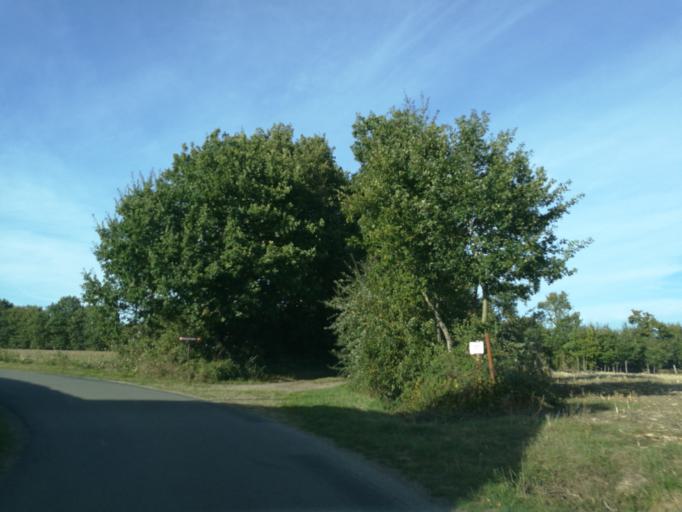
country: FR
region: Brittany
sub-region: Departement d'Ille-et-Vilaine
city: Bedee
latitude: 48.1976
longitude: -1.9524
